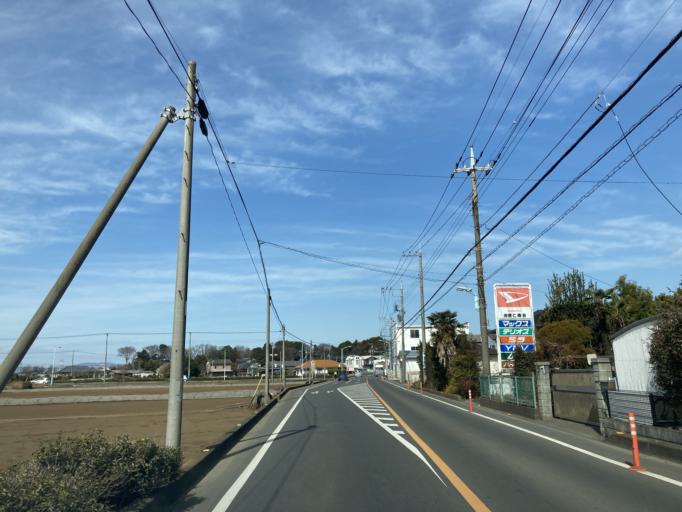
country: JP
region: Saitama
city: Tokorozawa
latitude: 35.8234
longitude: 139.4739
